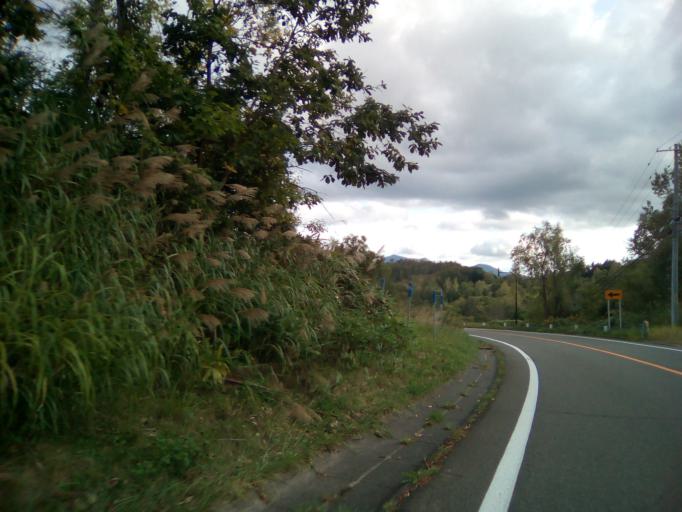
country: JP
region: Hokkaido
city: Niseko Town
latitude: 42.6604
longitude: 140.8241
